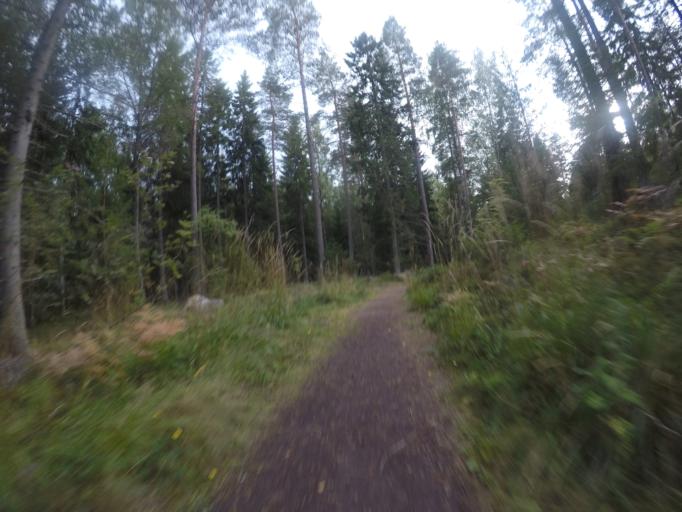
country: SE
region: Vaestmanland
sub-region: Vasteras
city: Vasteras
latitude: 59.6617
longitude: 16.5191
